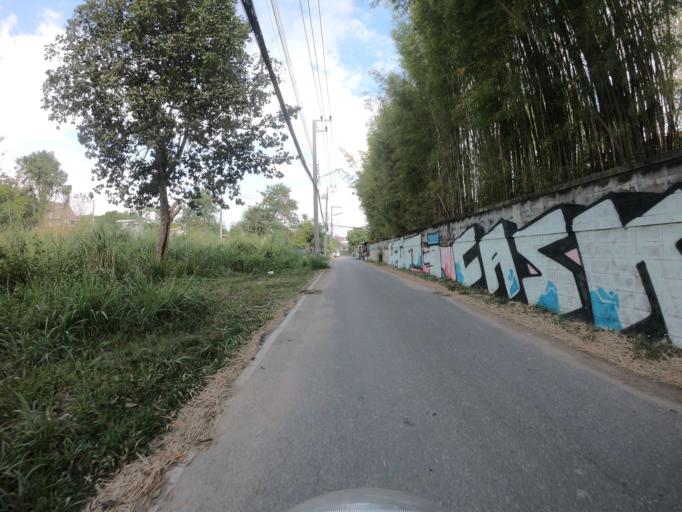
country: TH
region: Chiang Mai
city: Chiang Mai
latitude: 18.8158
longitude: 98.9714
